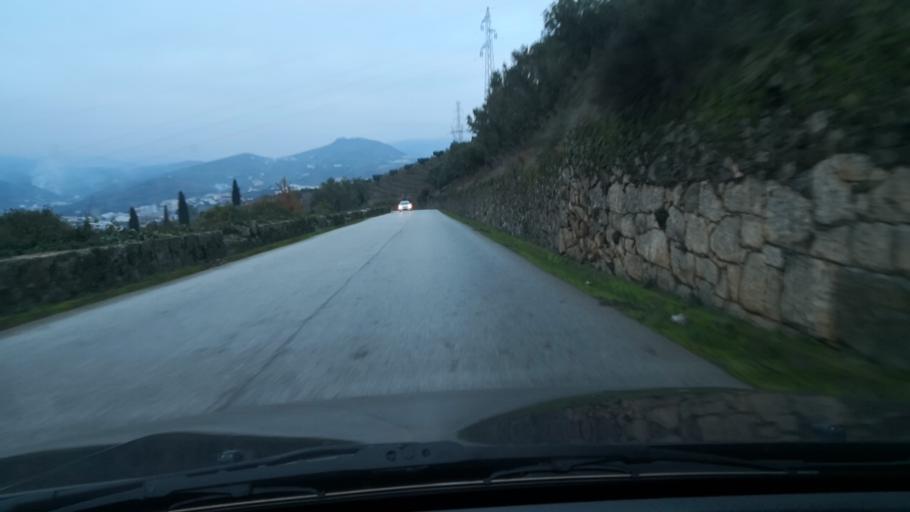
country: PT
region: Vila Real
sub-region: Peso da Regua
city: Peso da Regua
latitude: 41.1384
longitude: -7.7927
